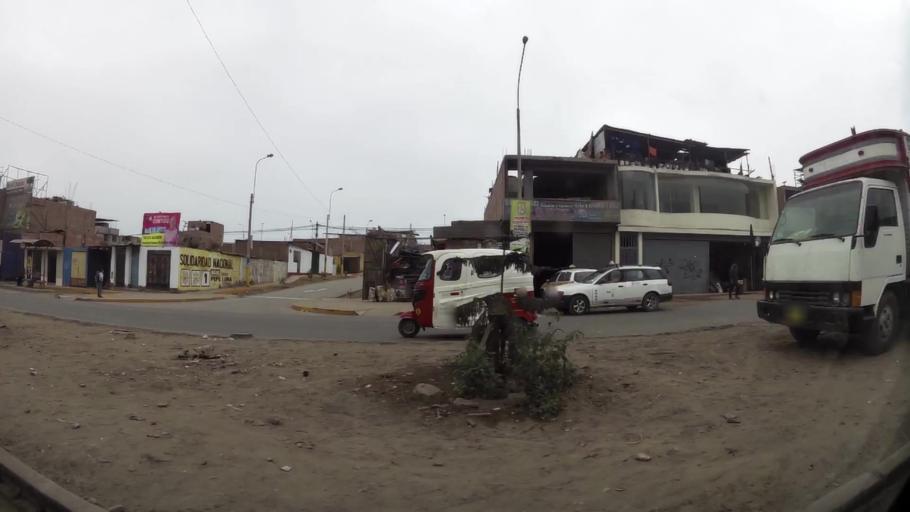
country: PE
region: Lima
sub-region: Lima
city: Surco
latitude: -12.2389
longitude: -76.9215
